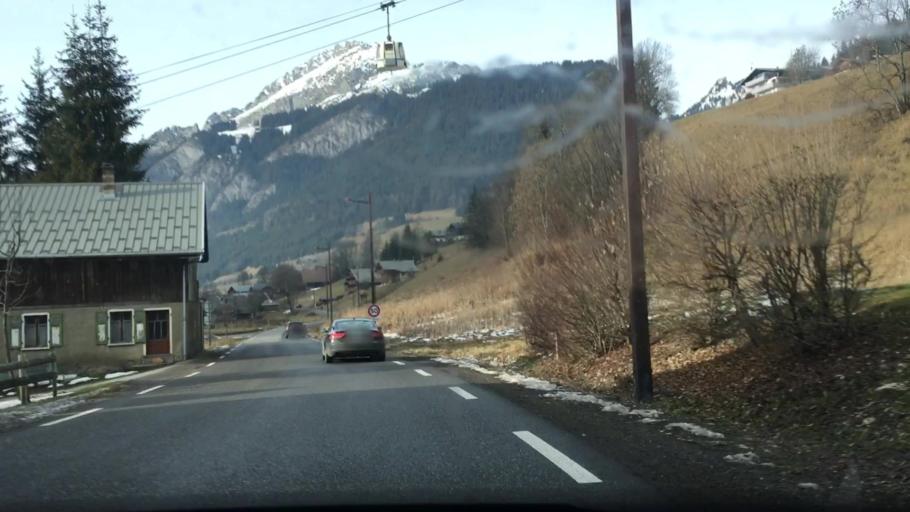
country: FR
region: Rhone-Alpes
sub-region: Departement de la Haute-Savoie
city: Chatel
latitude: 46.2915
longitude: 6.8011
